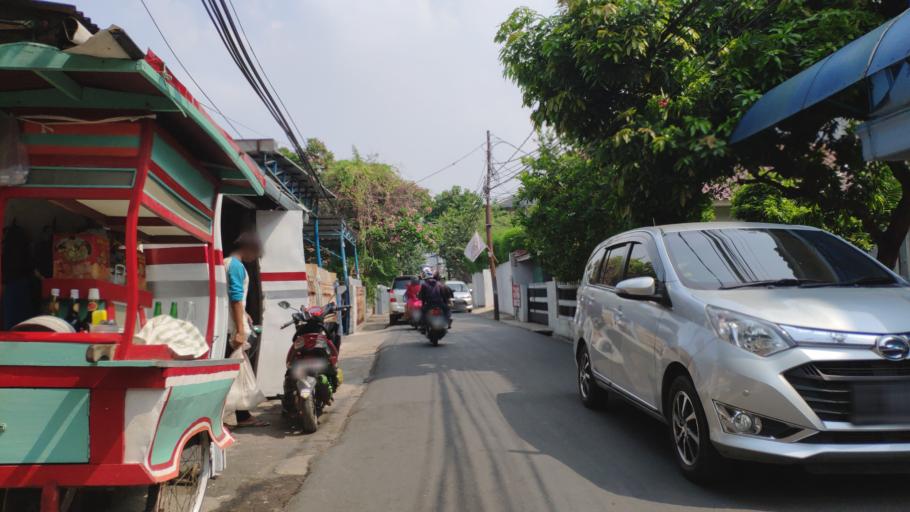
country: ID
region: Banten
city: South Tangerang
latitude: -6.2888
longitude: 106.7908
